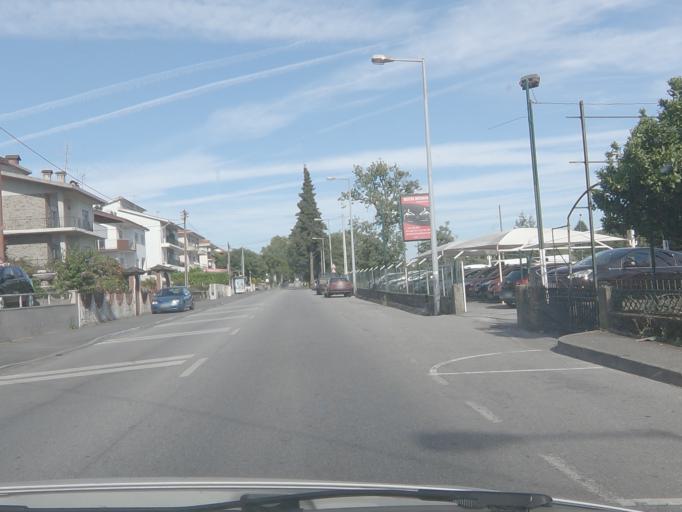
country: PT
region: Viseu
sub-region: Viseu
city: Viseu
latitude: 40.6543
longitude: -7.8943
